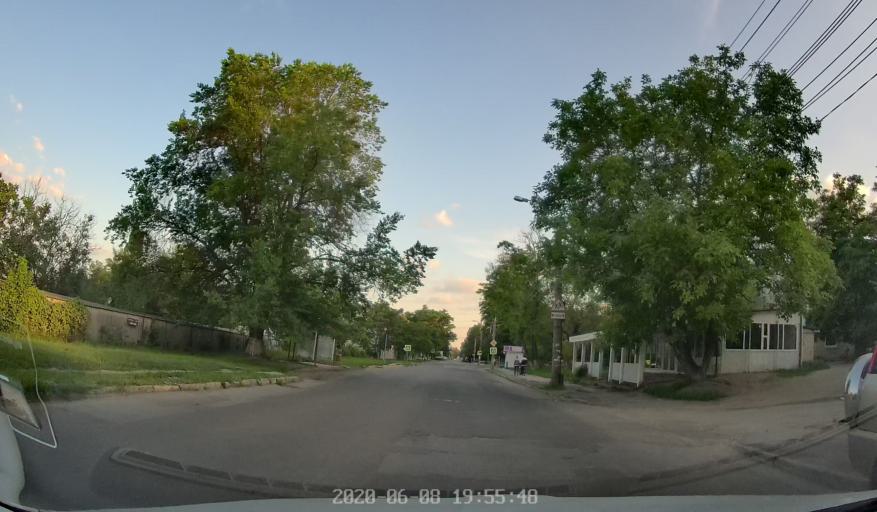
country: MD
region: Chisinau
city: Chisinau
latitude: 47.0264
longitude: 28.8836
